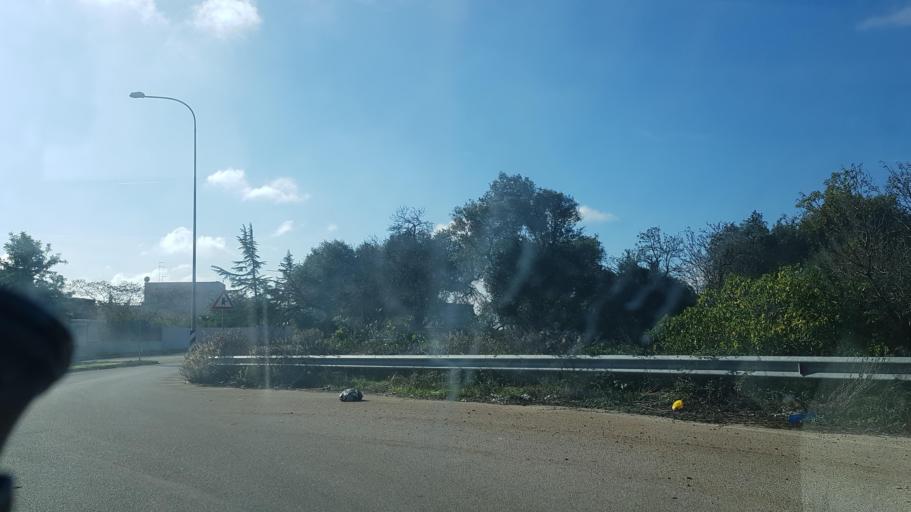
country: IT
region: Apulia
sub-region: Provincia di Brindisi
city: San Vito dei Normanni
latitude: 40.6719
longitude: 17.6997
